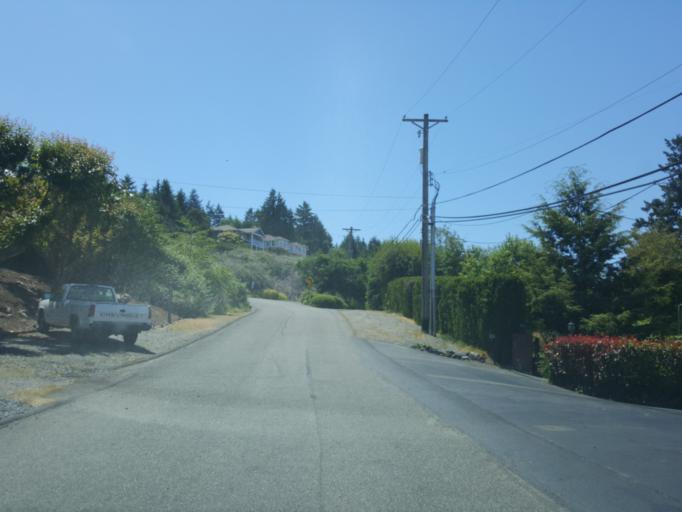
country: US
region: Washington
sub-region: Pierce County
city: University Place
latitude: 47.2159
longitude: -122.5722
